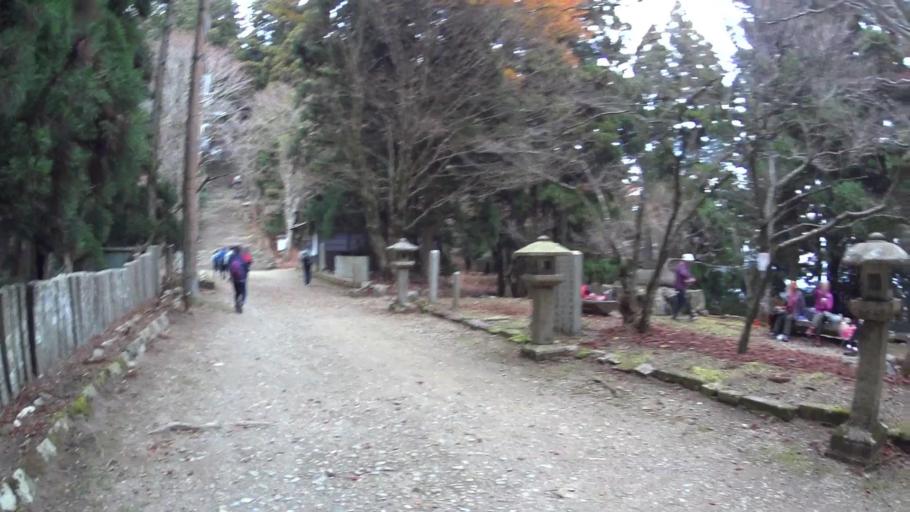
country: JP
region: Kyoto
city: Kameoka
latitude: 35.0581
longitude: 135.6347
